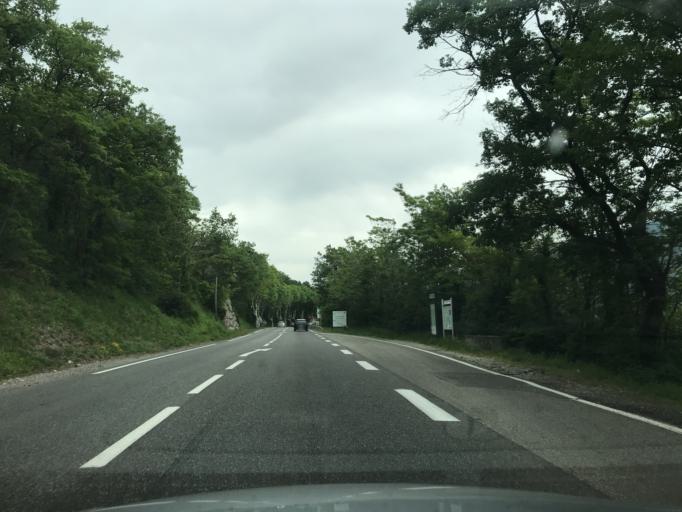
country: FR
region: Provence-Alpes-Cote d'Azur
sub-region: Departement des Alpes-de-Haute-Provence
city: Sisteron
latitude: 44.1702
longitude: 5.9489
